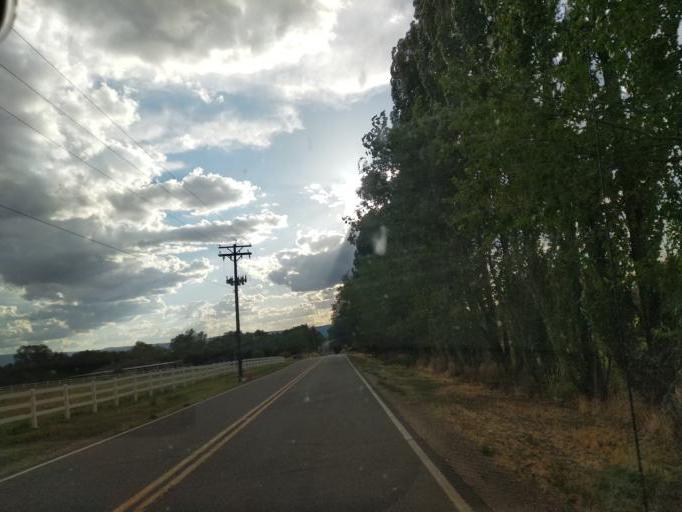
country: US
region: Colorado
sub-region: Mesa County
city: Clifton
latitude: 39.0558
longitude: -108.4233
